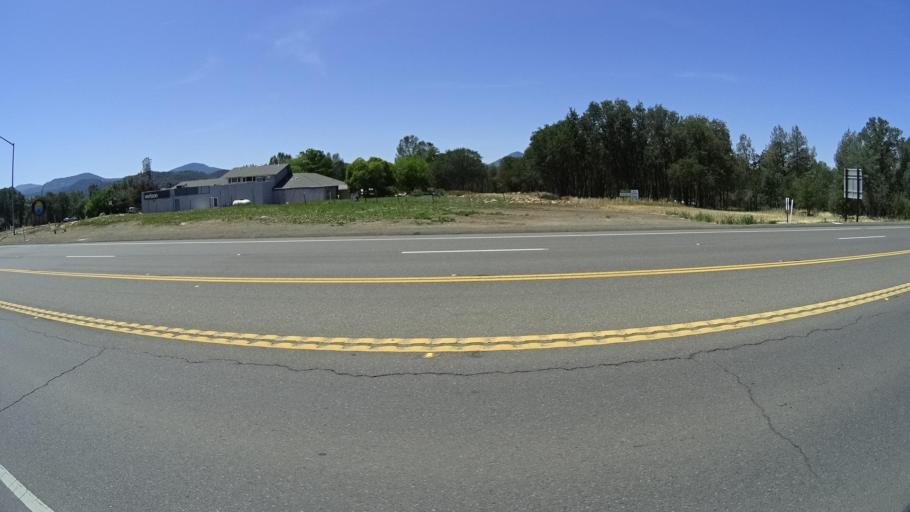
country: US
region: California
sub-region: Lake County
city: Clearlake
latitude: 38.9515
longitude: -122.6230
